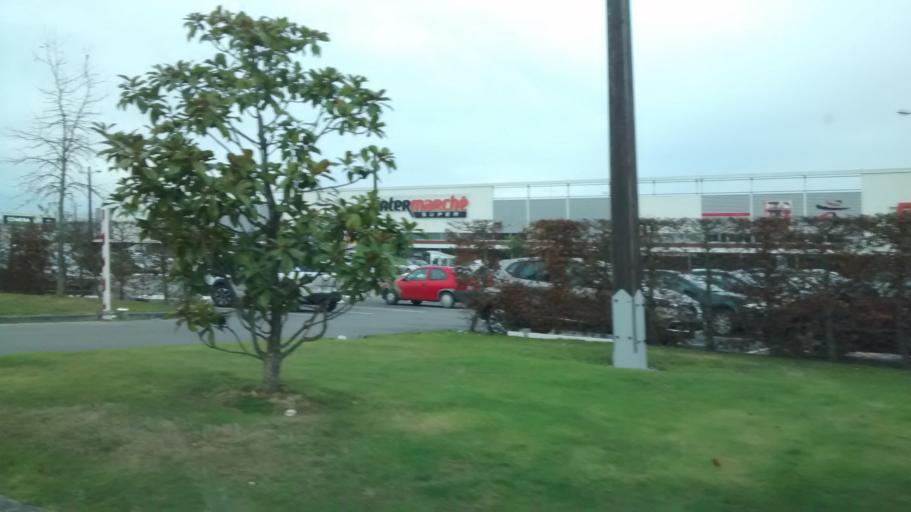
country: FR
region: Brittany
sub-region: Departement d'Ille-et-Vilaine
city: Liffre
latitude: 48.2238
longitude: -1.4998
